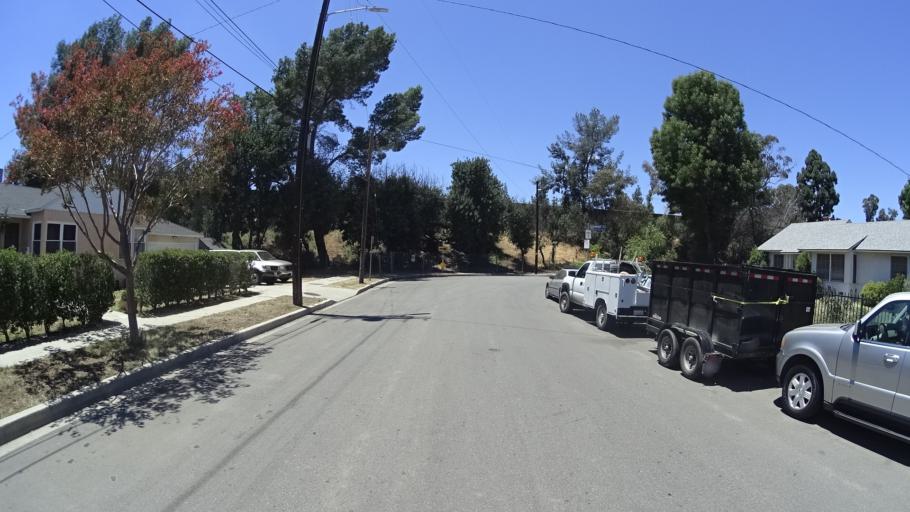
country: US
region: California
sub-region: Los Angeles County
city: Van Nuys
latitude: 34.2030
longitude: -118.4723
